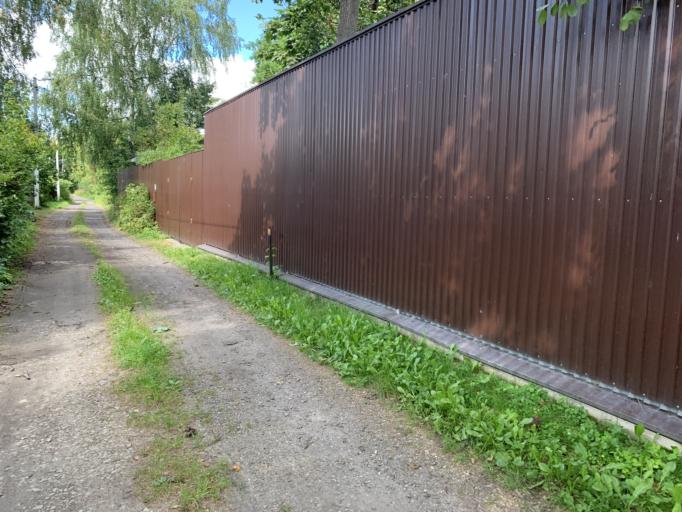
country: RU
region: Moskovskaya
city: Mamontovka
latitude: 55.9654
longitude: 37.8317
